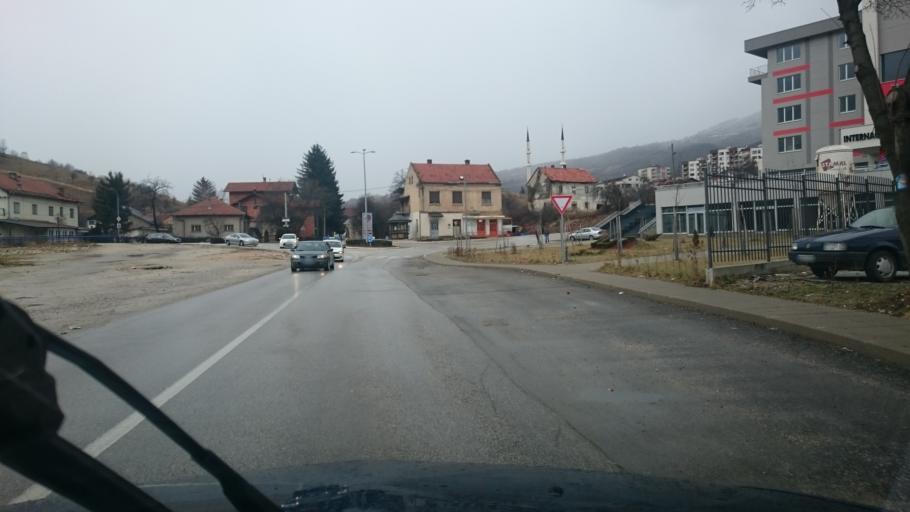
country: BA
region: Federation of Bosnia and Herzegovina
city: Travnik
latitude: 44.2264
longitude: 17.6467
